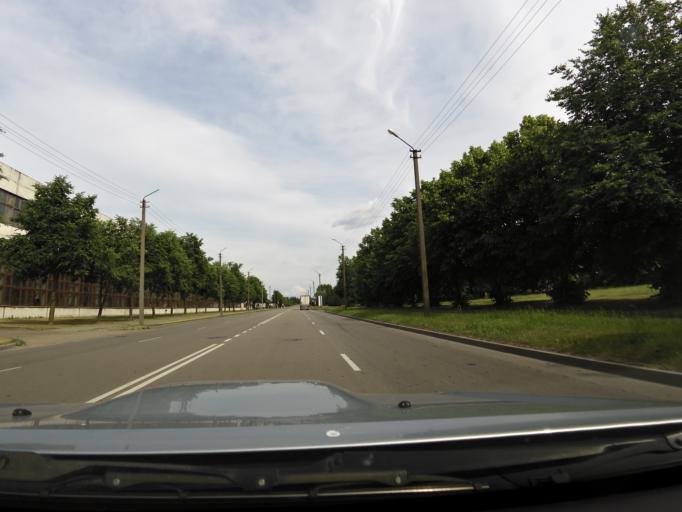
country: LT
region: Marijampoles apskritis
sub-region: Marijampole Municipality
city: Marijampole
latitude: 54.5749
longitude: 23.3734
